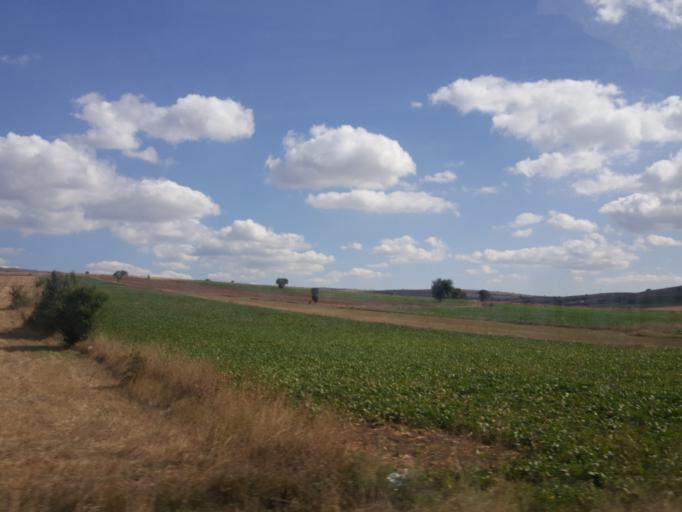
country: TR
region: Tokat
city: Camlibel
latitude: 40.1969
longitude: 36.4651
